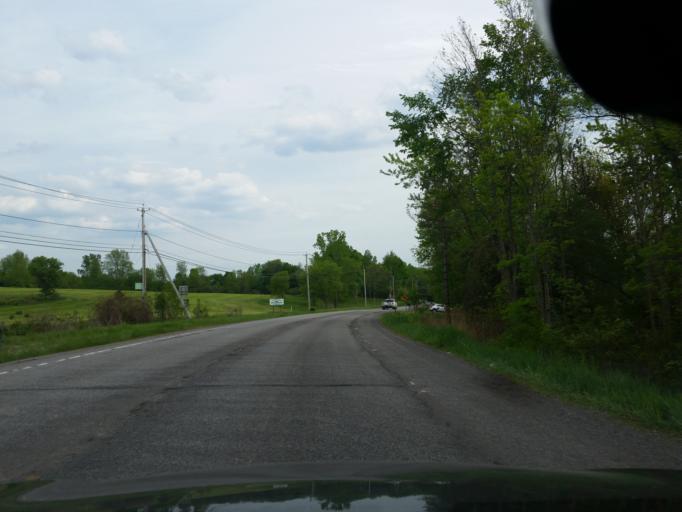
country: US
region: New York
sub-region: Chautauqua County
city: Mayville
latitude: 42.2333
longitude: -79.4398
